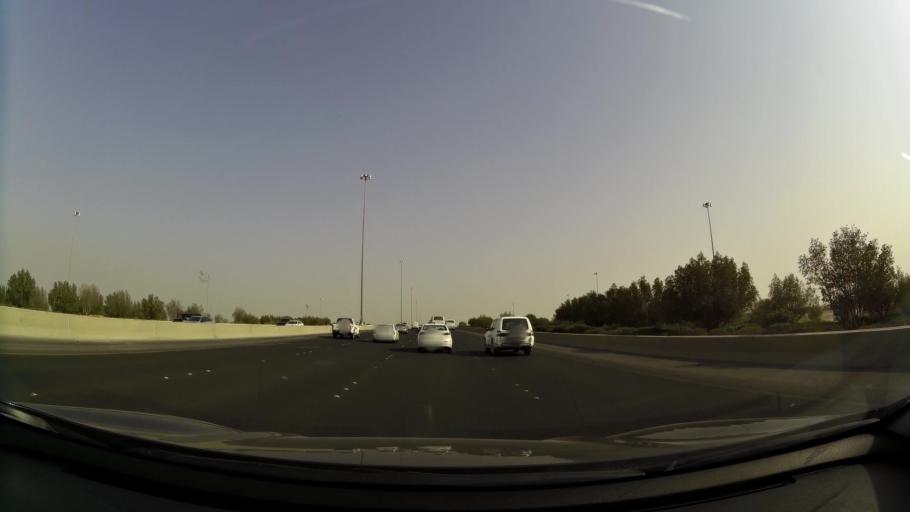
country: KW
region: Muhafazat al Jahra'
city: Al Jahra'
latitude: 29.3247
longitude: 47.7481
